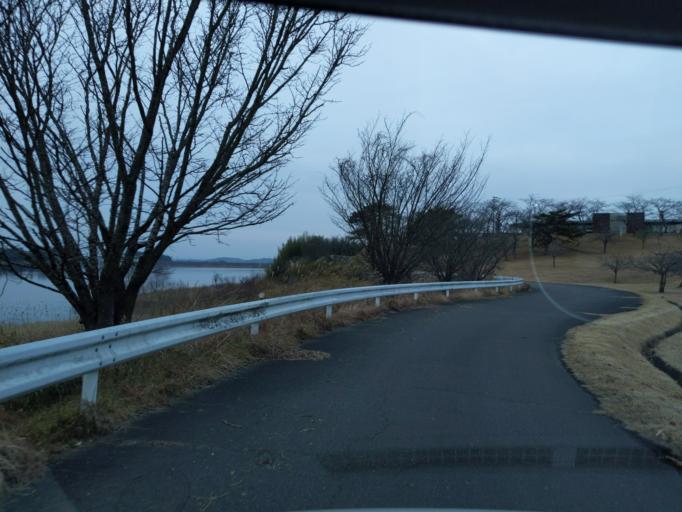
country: JP
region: Miyagi
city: Wakuya
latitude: 38.6990
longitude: 141.1456
